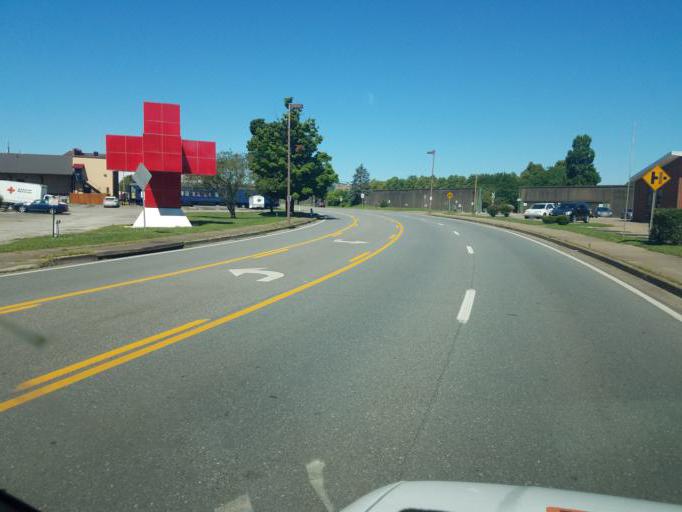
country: US
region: West Virginia
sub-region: Cabell County
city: Huntington
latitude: 38.4239
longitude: -82.4394
